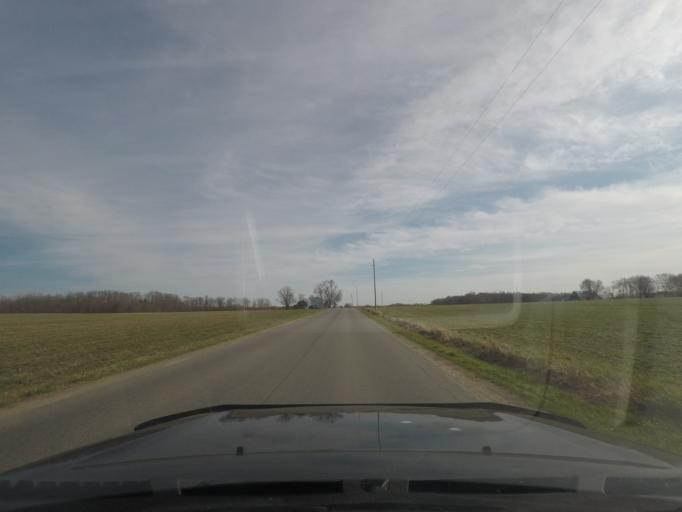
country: US
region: Indiana
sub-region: Elkhart County
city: Dunlap
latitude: 41.5643
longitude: -85.9249
